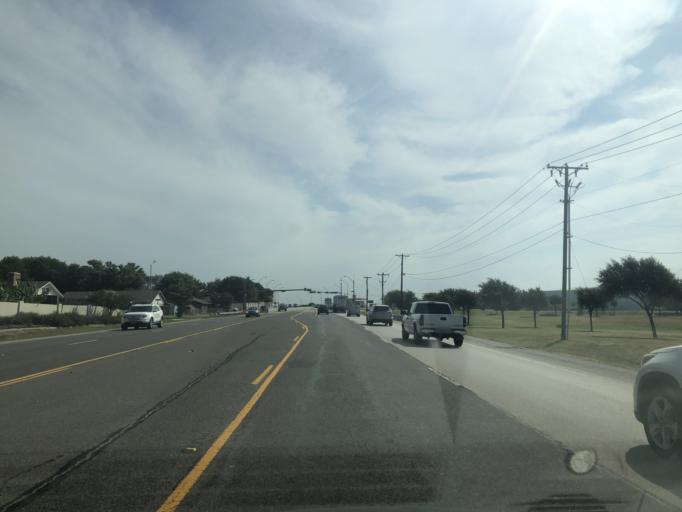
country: US
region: Texas
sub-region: Tarrant County
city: Benbrook
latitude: 32.6676
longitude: -97.4762
